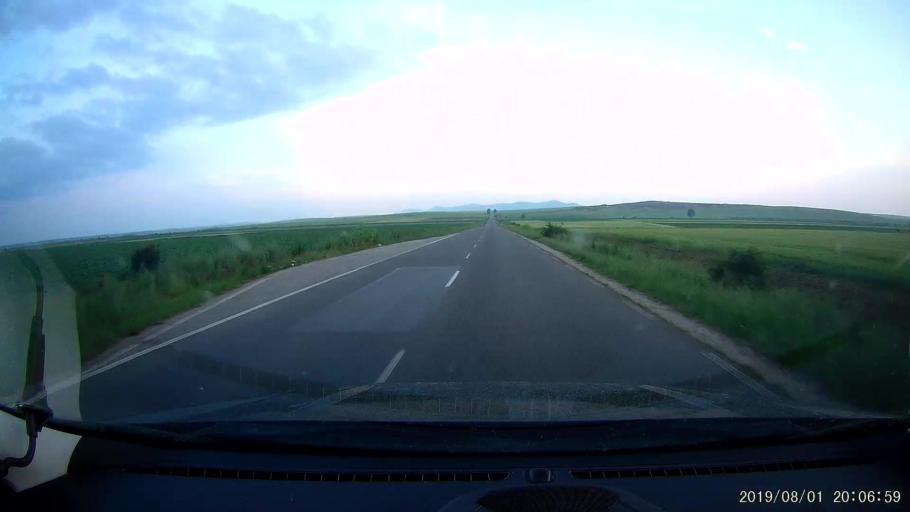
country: BG
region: Yambol
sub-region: Obshtina Yambol
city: Yambol
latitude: 42.5287
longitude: 26.5606
